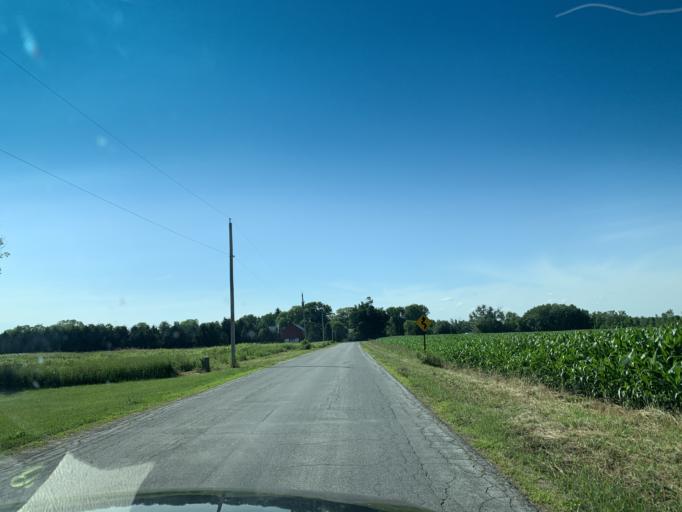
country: US
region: New York
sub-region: Madison County
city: Oneida
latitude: 43.1535
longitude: -75.6669
